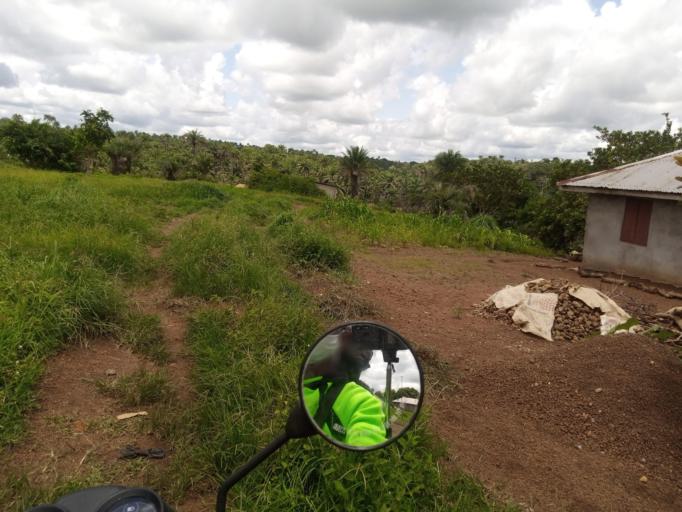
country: SL
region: Northern Province
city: Port Loko
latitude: 8.7584
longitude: -12.7758
